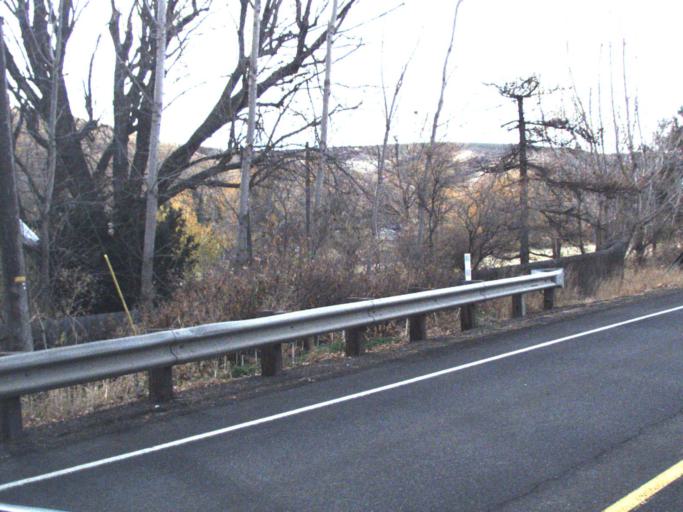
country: US
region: Washington
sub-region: Garfield County
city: Pomeroy
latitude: 46.4739
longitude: -117.5425
